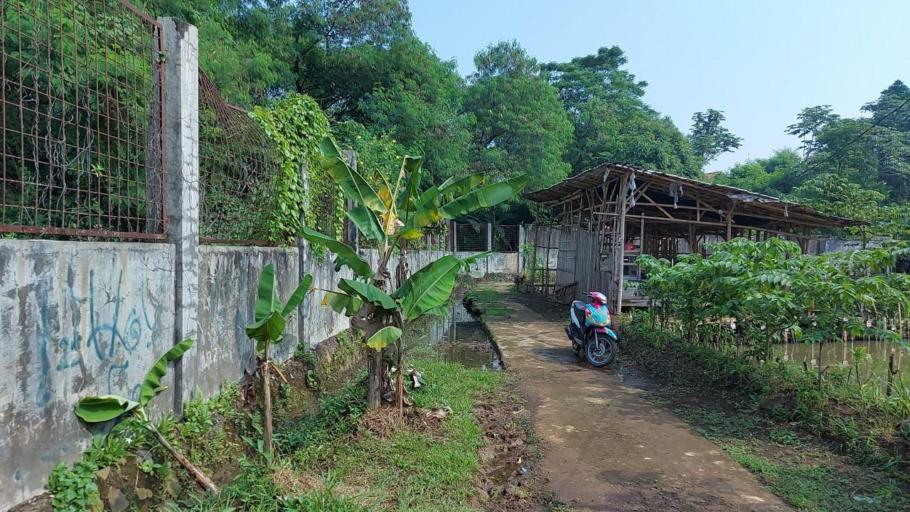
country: ID
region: West Java
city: Cibinong
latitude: -6.5263
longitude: 106.8358
